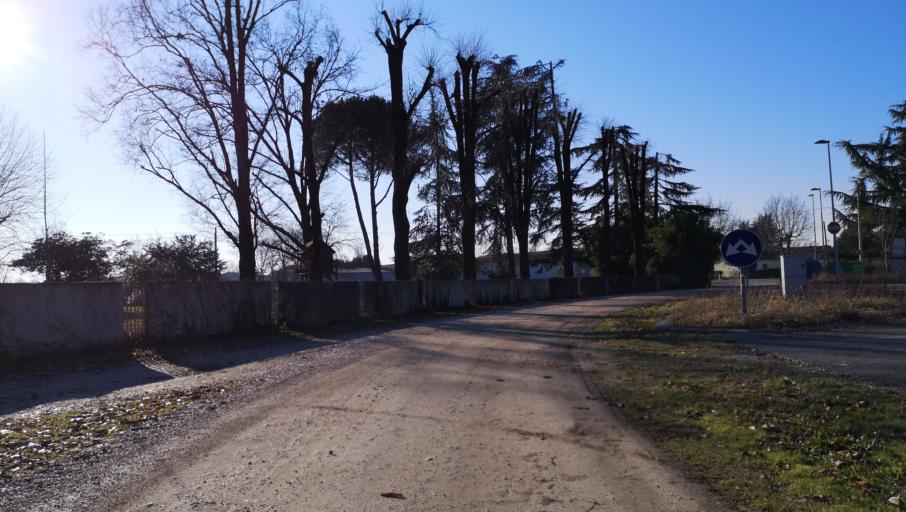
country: IT
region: Friuli Venezia Giulia
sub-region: Provincia di Udine
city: Palmanova
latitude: 45.9127
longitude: 13.2993
